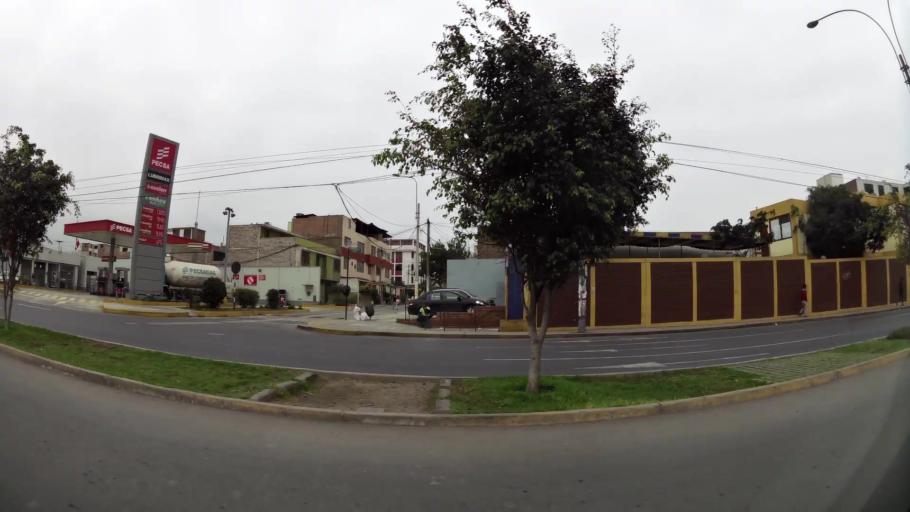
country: PE
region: Callao
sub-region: Callao
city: Callao
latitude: -12.0515
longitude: -77.0782
